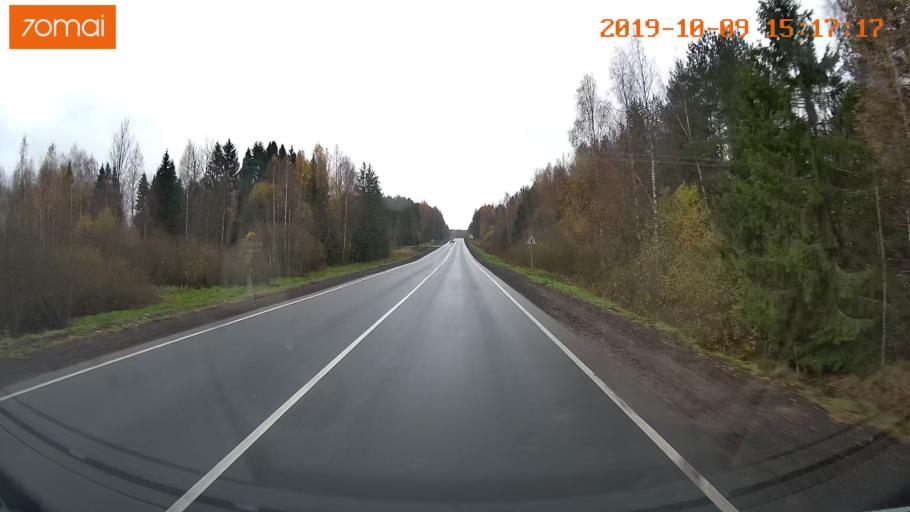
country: RU
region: Kostroma
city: Susanino
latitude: 58.1004
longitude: 41.5833
